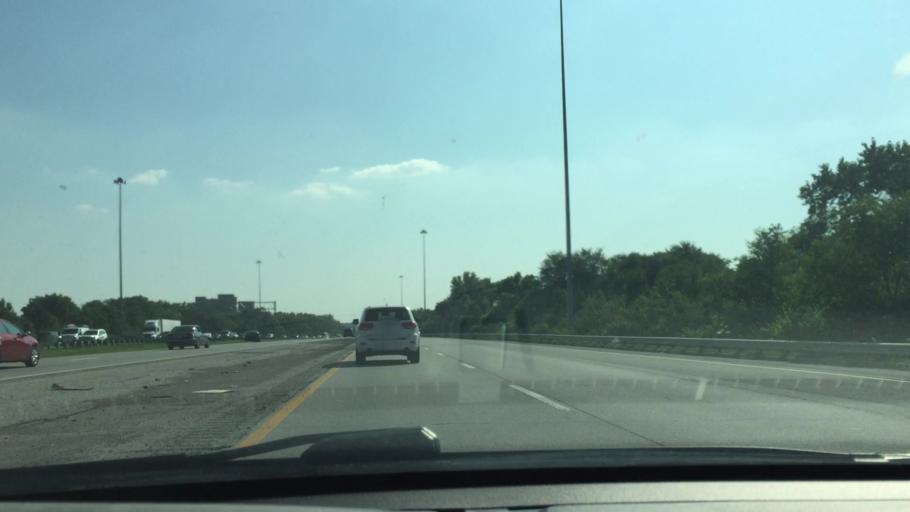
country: US
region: Ohio
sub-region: Franklin County
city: Blacklick Estates
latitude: 39.9301
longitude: -82.8594
